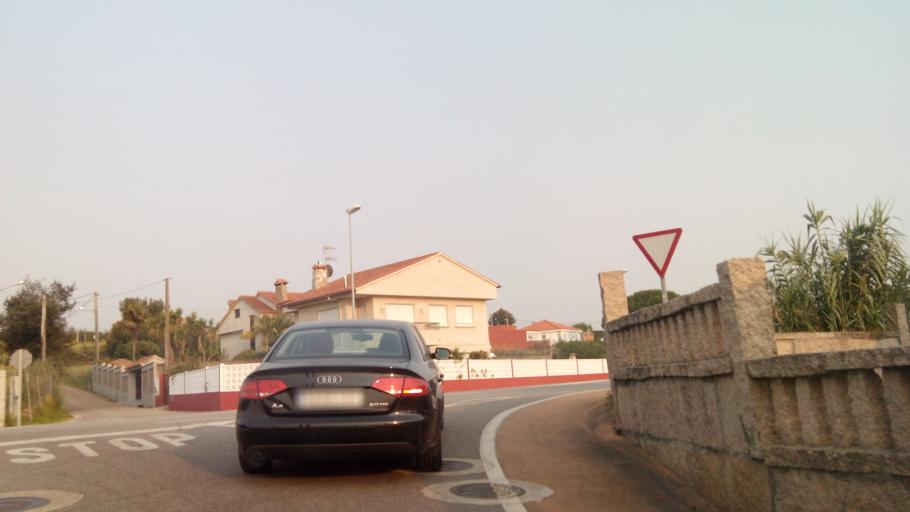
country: ES
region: Galicia
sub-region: Provincia de Pontevedra
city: Nigran
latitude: 42.1479
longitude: -8.8221
